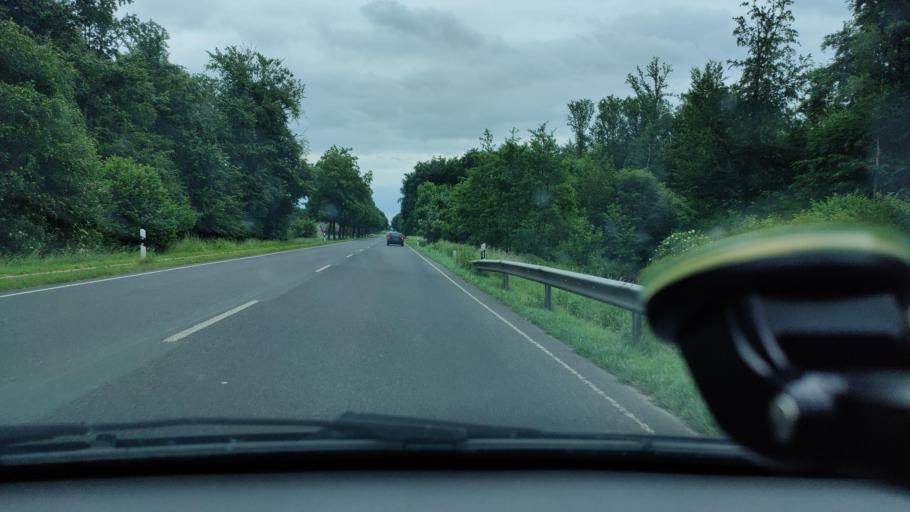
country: DE
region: North Rhine-Westphalia
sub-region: Regierungsbezirk Dusseldorf
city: Weeze
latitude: 51.6650
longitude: 6.2343
